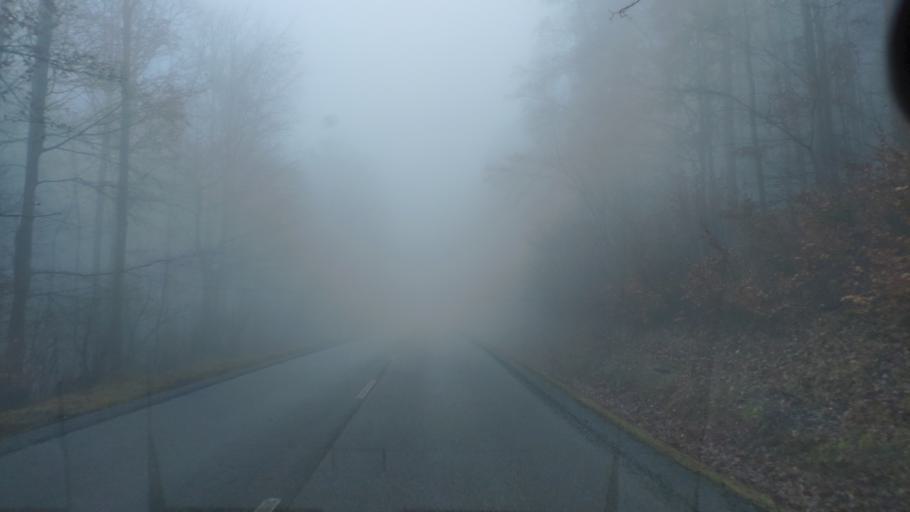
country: SK
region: Banskobystricky
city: Revuca
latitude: 48.6450
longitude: 20.2882
